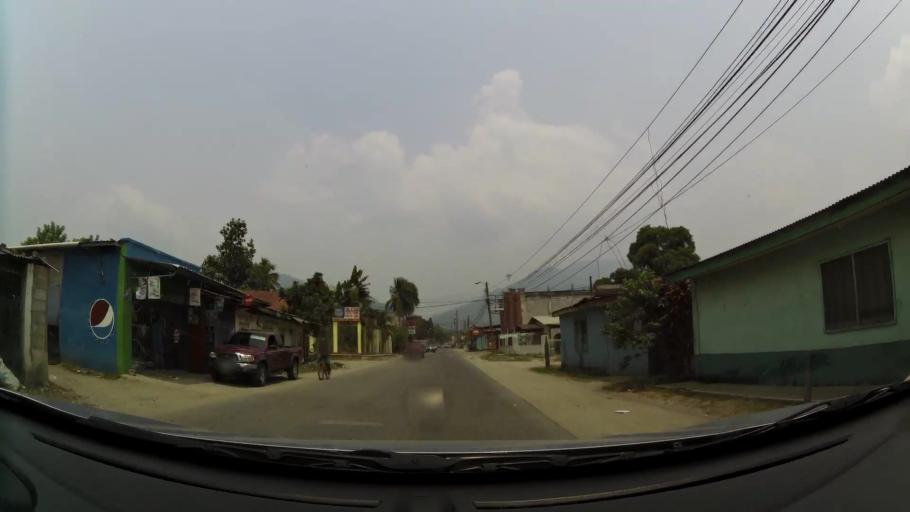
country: HN
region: Yoro
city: El Progreso
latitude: 15.3987
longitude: -87.8024
